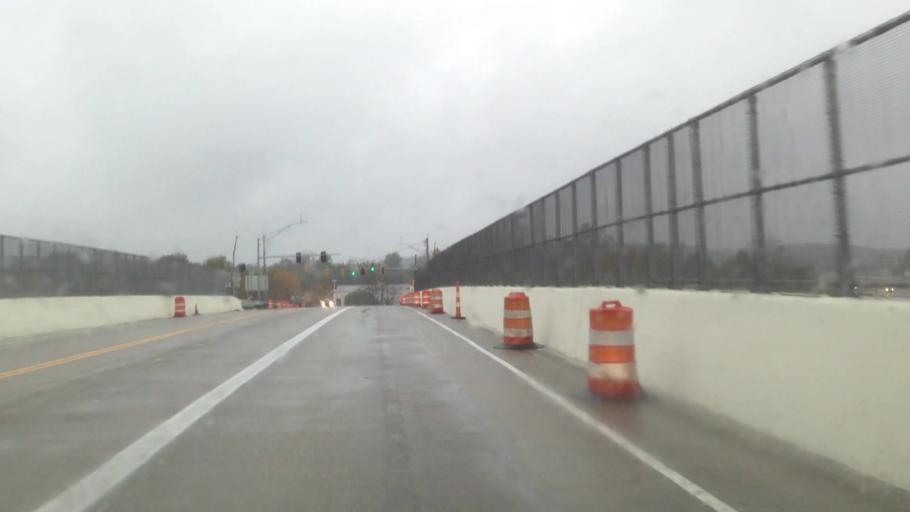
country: US
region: Ohio
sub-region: Portage County
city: Streetsboro
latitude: 41.2618
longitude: -81.3776
